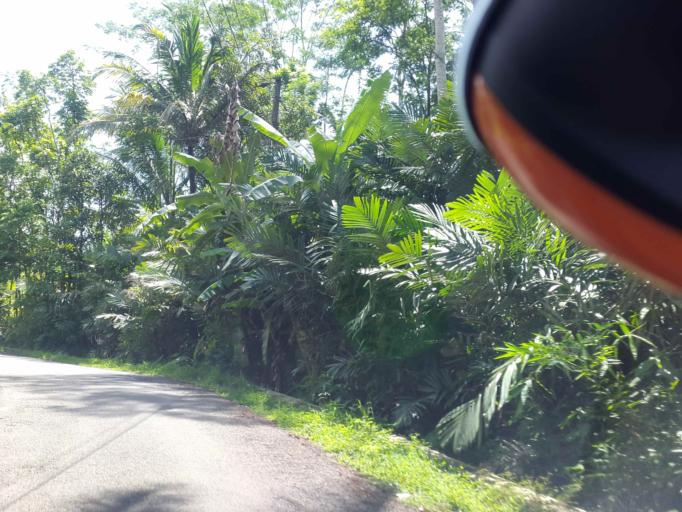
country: ID
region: Central Java
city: Wonosobo
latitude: -7.3565
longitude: 109.6787
